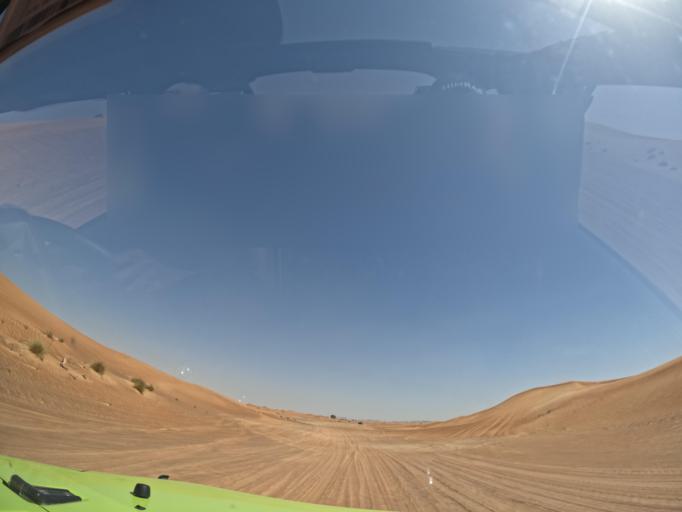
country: AE
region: Ash Shariqah
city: Adh Dhayd
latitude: 25.0025
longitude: 55.7317
